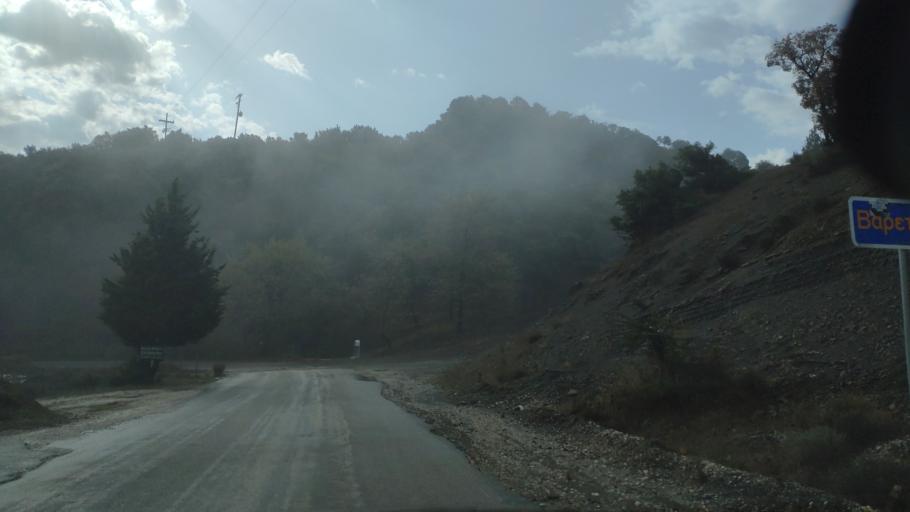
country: GR
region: West Greece
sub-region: Nomos Aitolias kai Akarnanias
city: Sardinia
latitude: 38.8702
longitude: 21.2823
